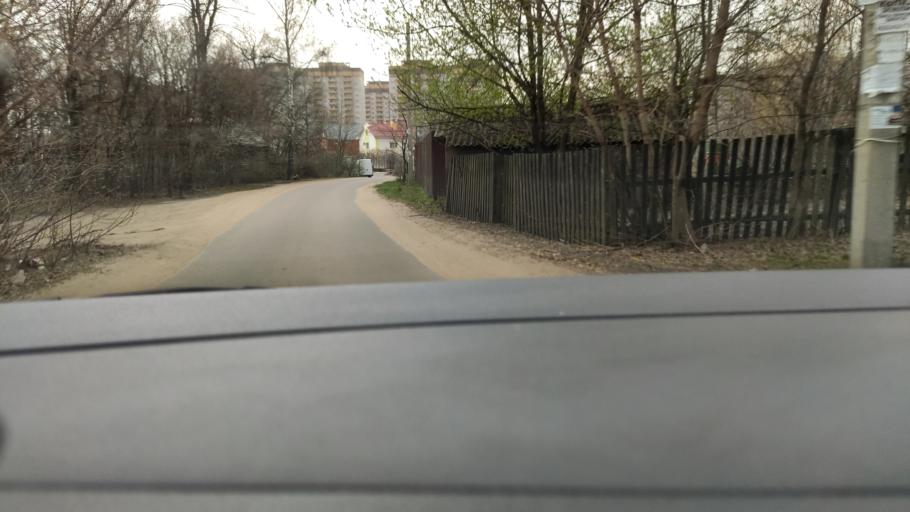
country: RU
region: Voronezj
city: Podgornoye
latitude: 51.7360
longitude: 39.1873
